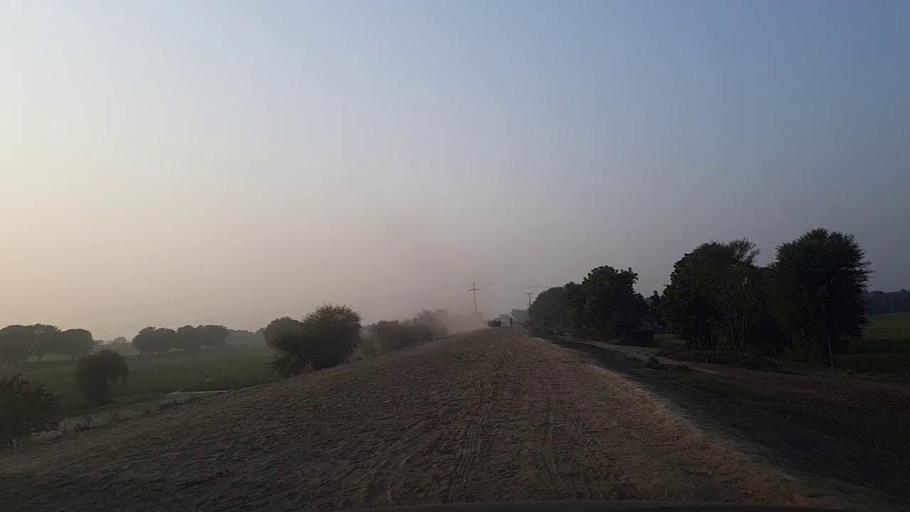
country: PK
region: Sindh
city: Sann
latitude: 26.1738
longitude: 68.1017
